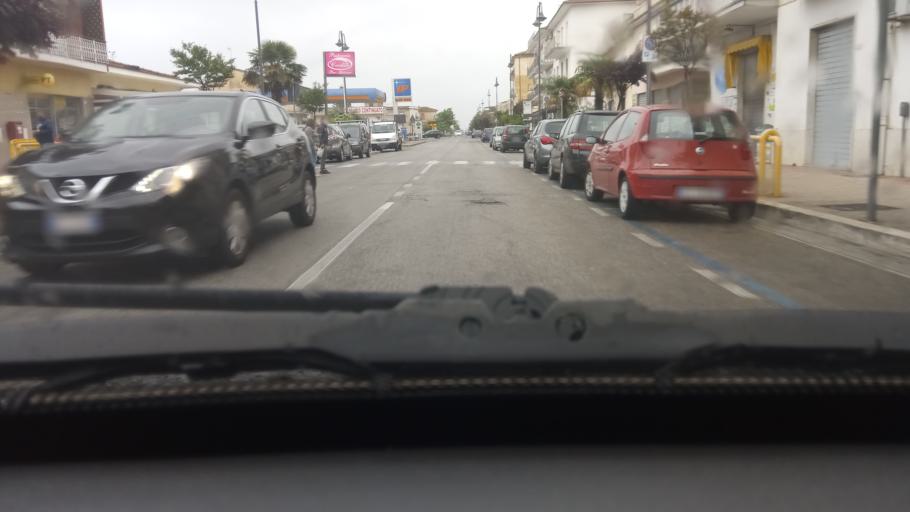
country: IT
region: Latium
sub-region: Provincia di Latina
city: Minturno
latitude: 41.2491
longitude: 13.7396
